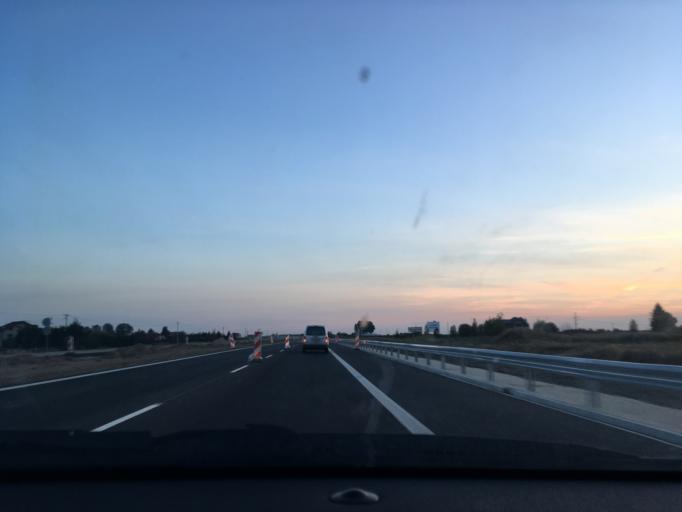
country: PL
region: Podlasie
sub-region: Powiat zambrowski
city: Zambrow
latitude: 52.9592
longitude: 22.1916
